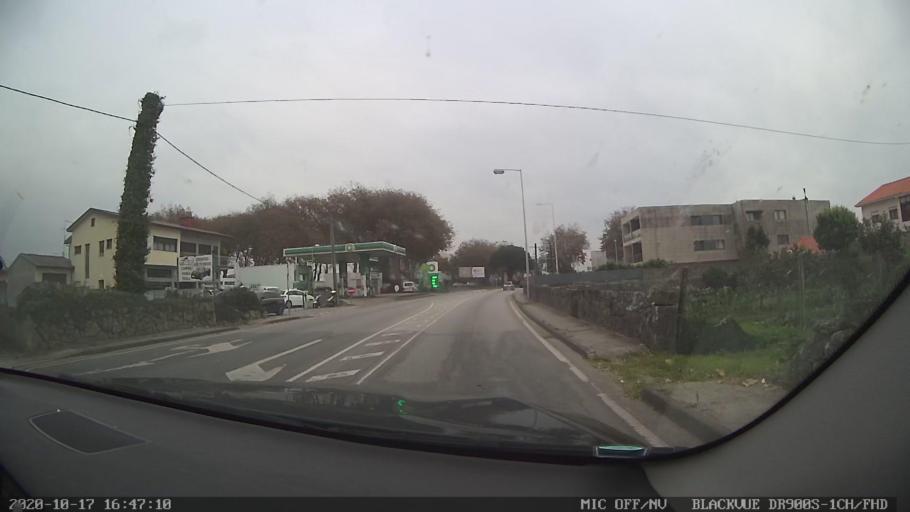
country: PT
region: Braga
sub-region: Esposende
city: Esposende
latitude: 41.5323
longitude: -8.7764
